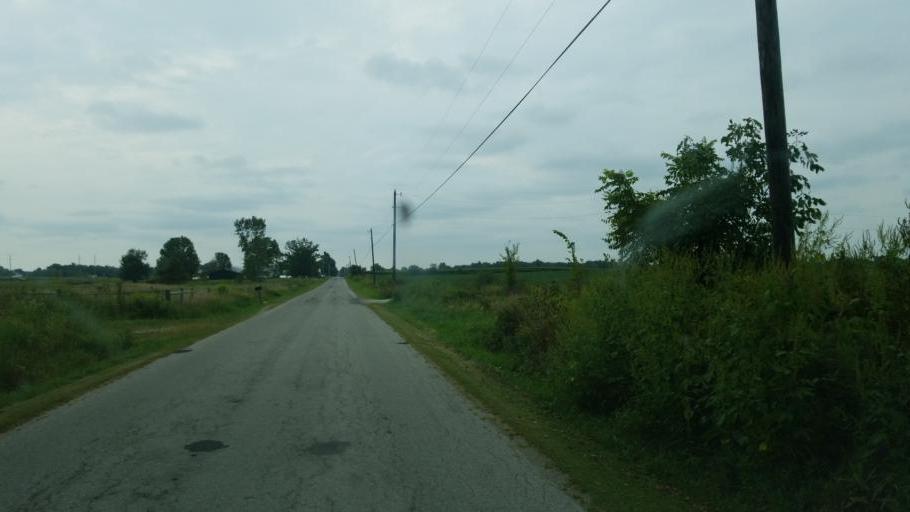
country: US
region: Ohio
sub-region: Morrow County
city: Mount Gilead
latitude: 40.6316
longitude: -82.8418
